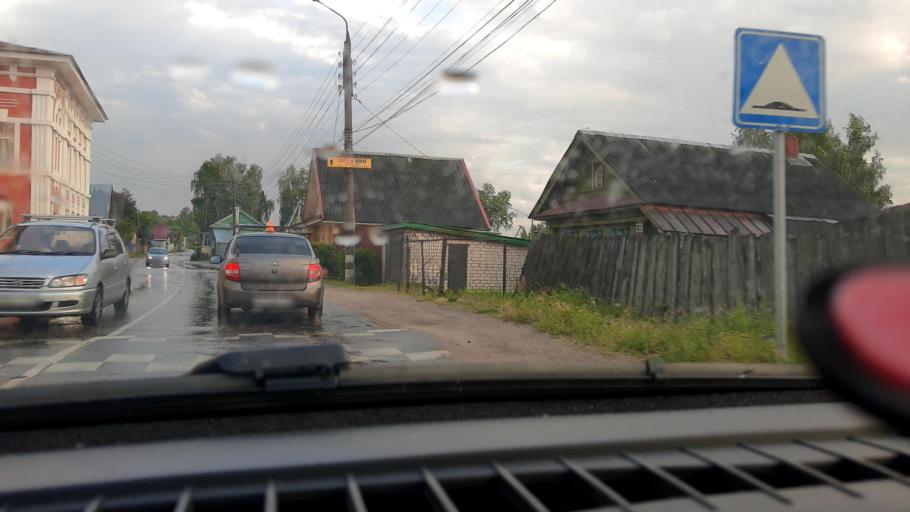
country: RU
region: Nizjnij Novgorod
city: Gorodets
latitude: 56.6551
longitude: 43.4643
